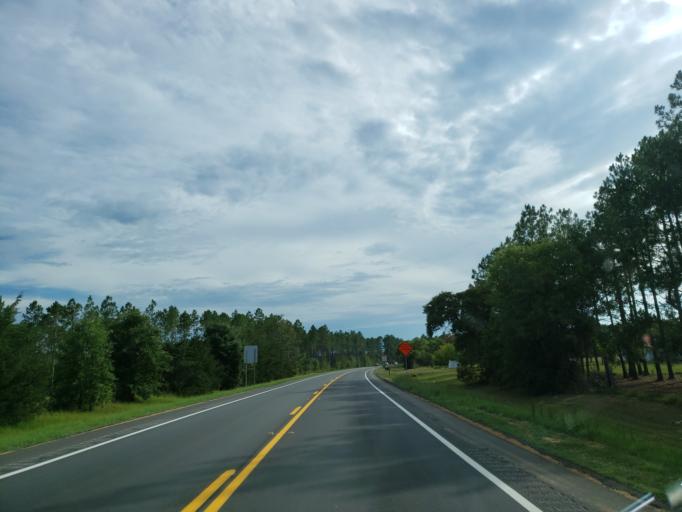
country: US
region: Georgia
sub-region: Berrien County
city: Enigma
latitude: 31.5421
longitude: -83.3850
